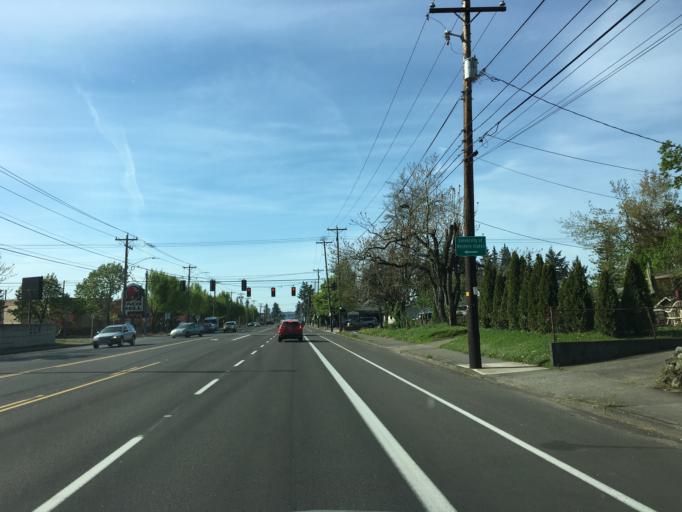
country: US
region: Oregon
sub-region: Multnomah County
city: Lents
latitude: 45.5380
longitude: -122.5377
